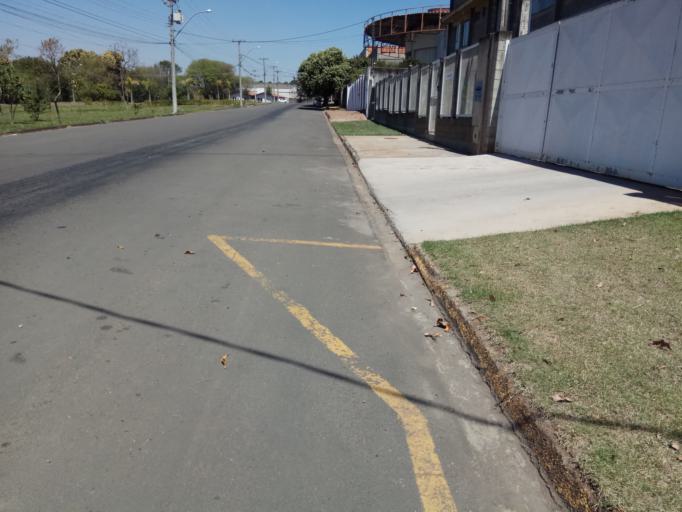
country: BR
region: Sao Paulo
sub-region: Piracicaba
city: Piracicaba
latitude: -22.7312
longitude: -47.5938
